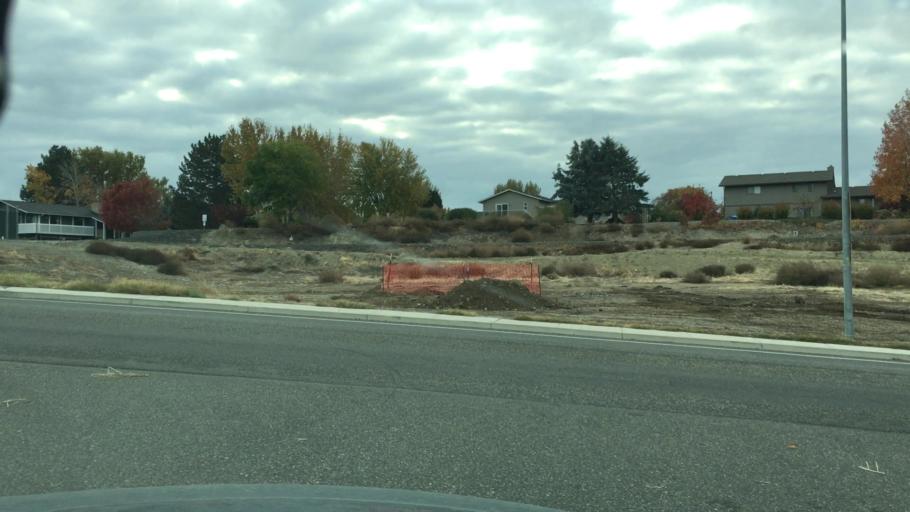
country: US
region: Washington
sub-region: Franklin County
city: West Pasco
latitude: 46.1890
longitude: -119.1976
